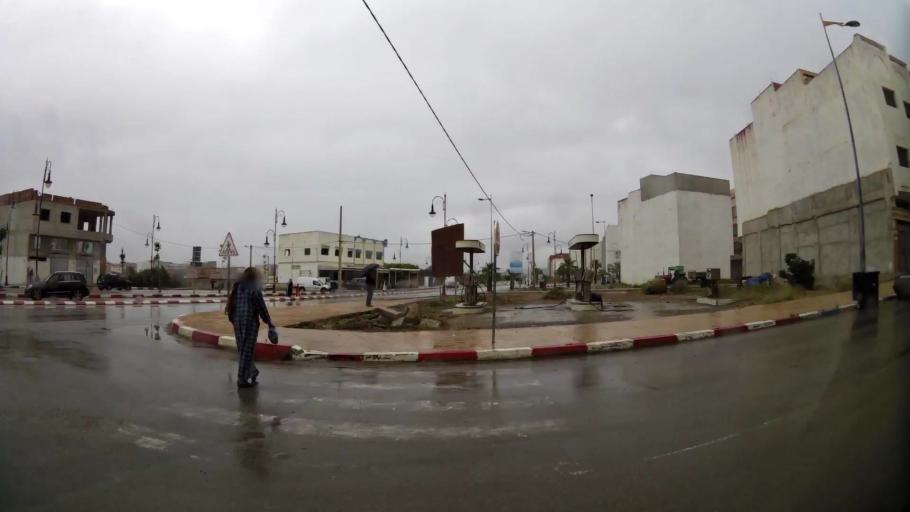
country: MA
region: Taza-Al Hoceima-Taounate
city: Imzourene
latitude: 35.1427
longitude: -3.8485
